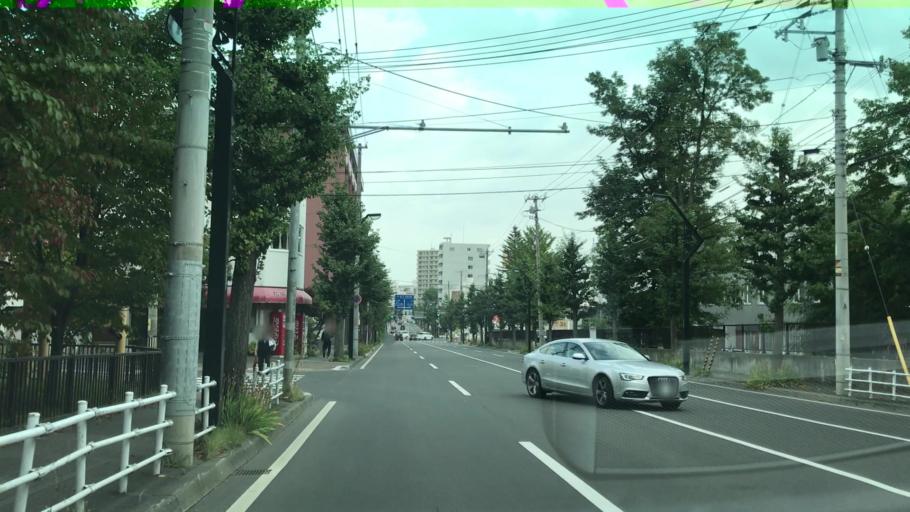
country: JP
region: Hokkaido
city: Sapporo
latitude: 43.0451
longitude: 141.3212
